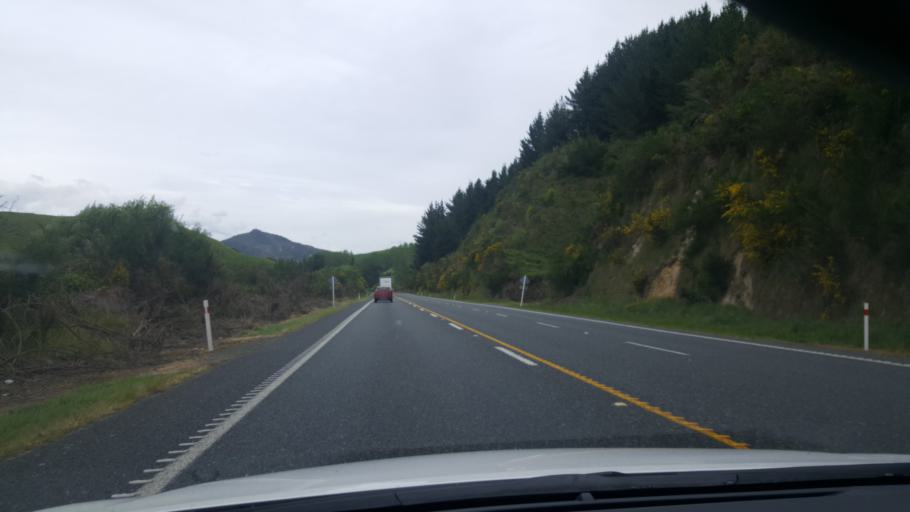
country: NZ
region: Bay of Plenty
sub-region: Rotorua District
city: Rotorua
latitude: -38.2915
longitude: 176.3536
